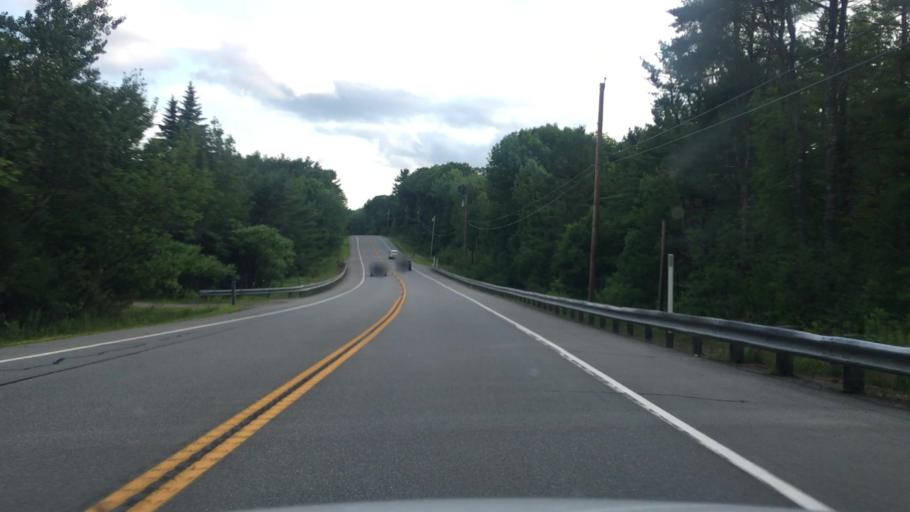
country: US
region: Maine
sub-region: Kennebec County
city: Windsor
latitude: 44.3611
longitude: -69.6395
